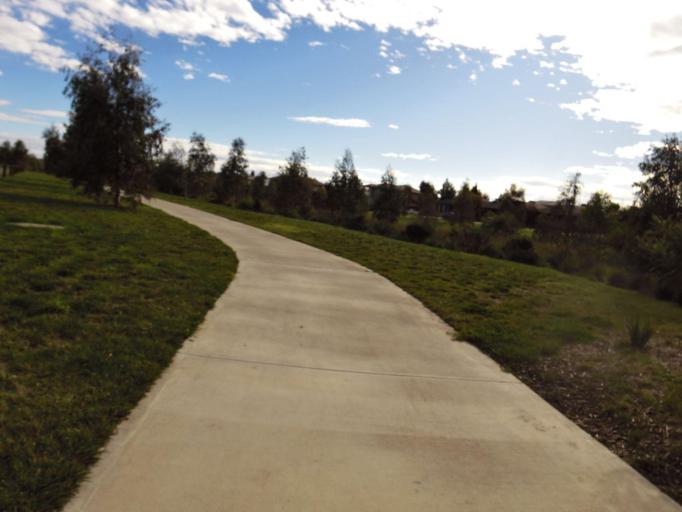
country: AU
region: Victoria
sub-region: Whittlesea
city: Epping
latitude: -37.6138
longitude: 145.0410
